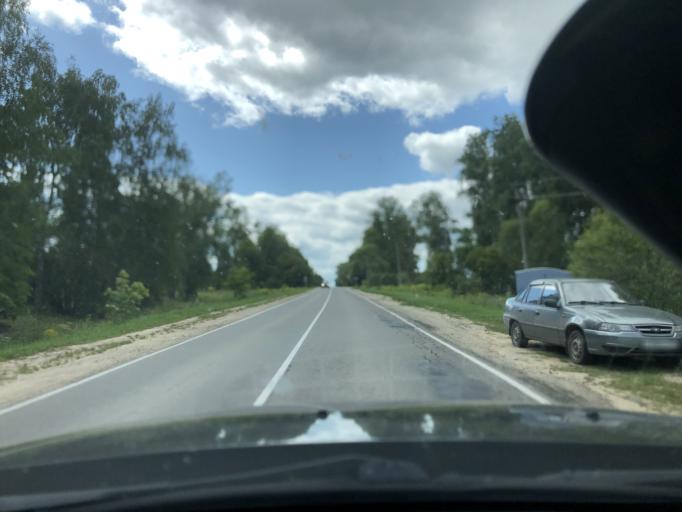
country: RU
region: Tula
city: Revyakino
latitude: 54.3519
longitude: 37.6281
